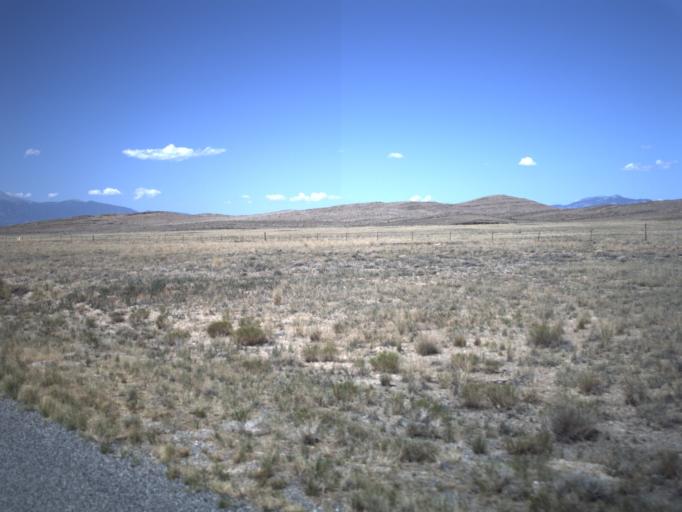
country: US
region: Utah
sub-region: Beaver County
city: Milford
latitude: 39.0462
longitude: -113.7962
